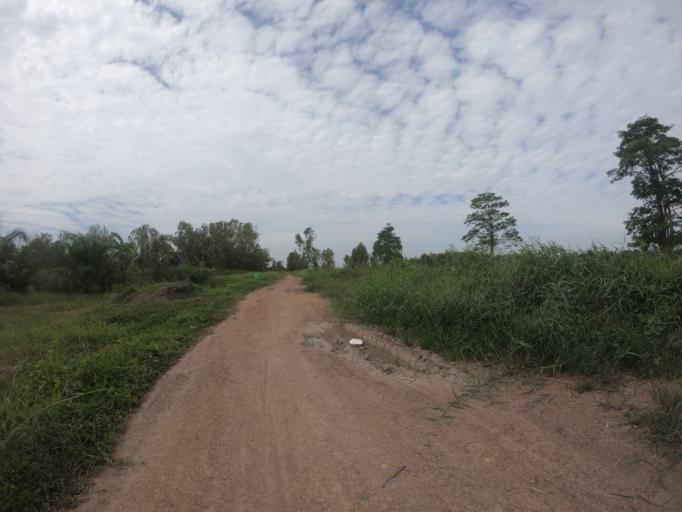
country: TH
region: Pathum Thani
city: Ban Lam Luk Ka
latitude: 14.0337
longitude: 100.8568
